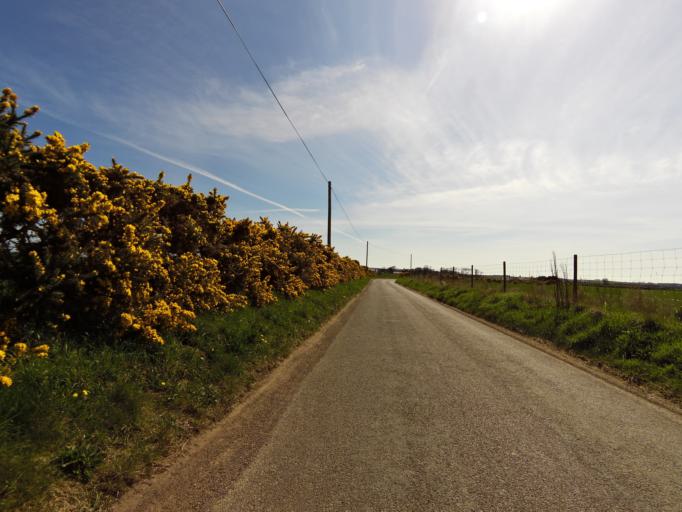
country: GB
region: Scotland
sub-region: Angus
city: Montrose
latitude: 56.6478
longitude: -2.5137
